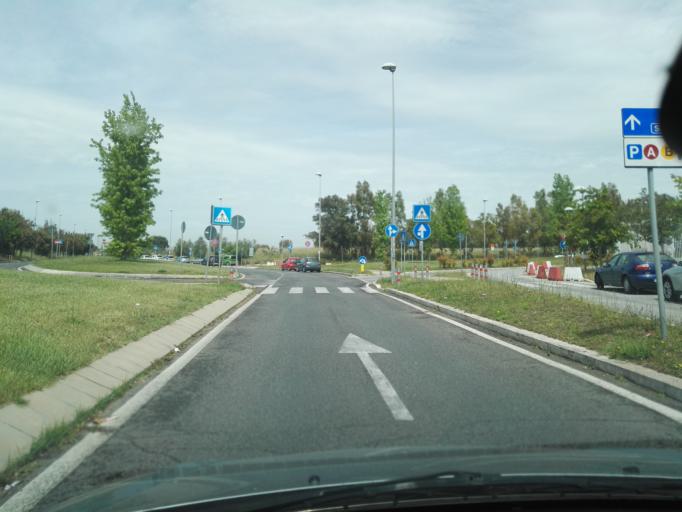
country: IT
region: Latium
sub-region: Citta metropolitana di Roma Capitale
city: Selcetta
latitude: 41.7711
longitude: 12.4662
